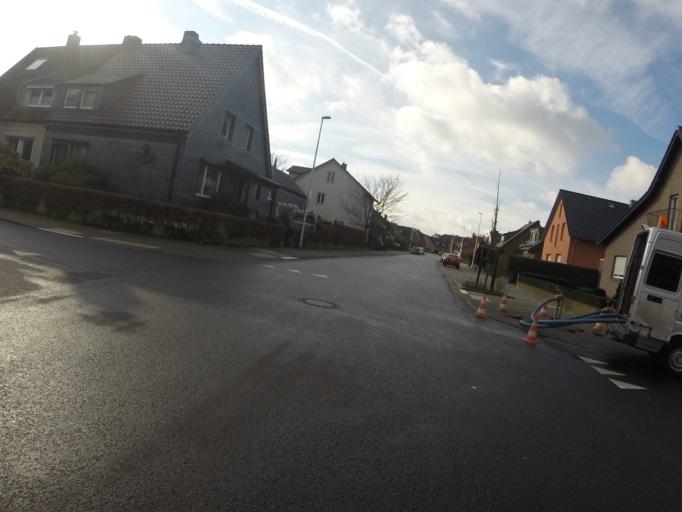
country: DE
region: North Rhine-Westphalia
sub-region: Regierungsbezirk Koln
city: Herzogenrath
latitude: 50.8379
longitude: 6.0895
